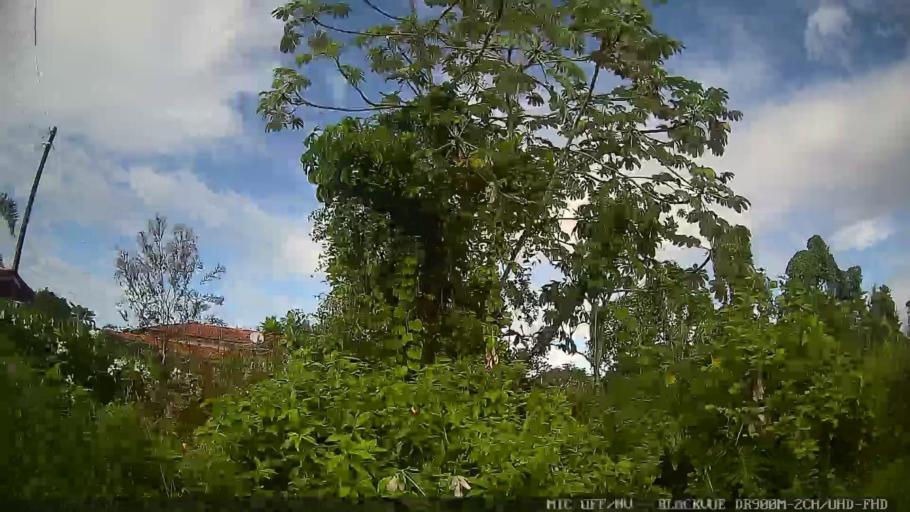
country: BR
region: Sao Paulo
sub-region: Itanhaem
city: Itanhaem
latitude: -24.2306
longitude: -46.8907
